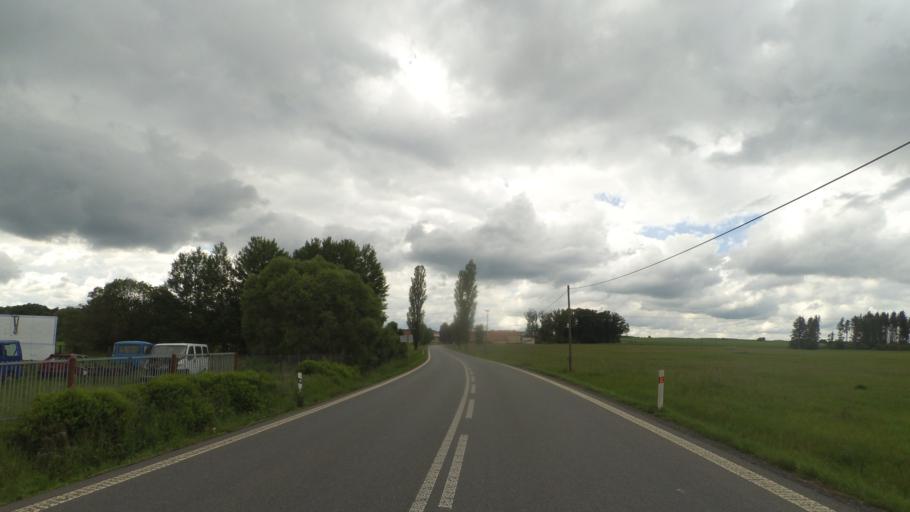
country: CZ
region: Plzensky
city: Horsovsky Tyn
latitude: 49.5412
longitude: 12.9205
